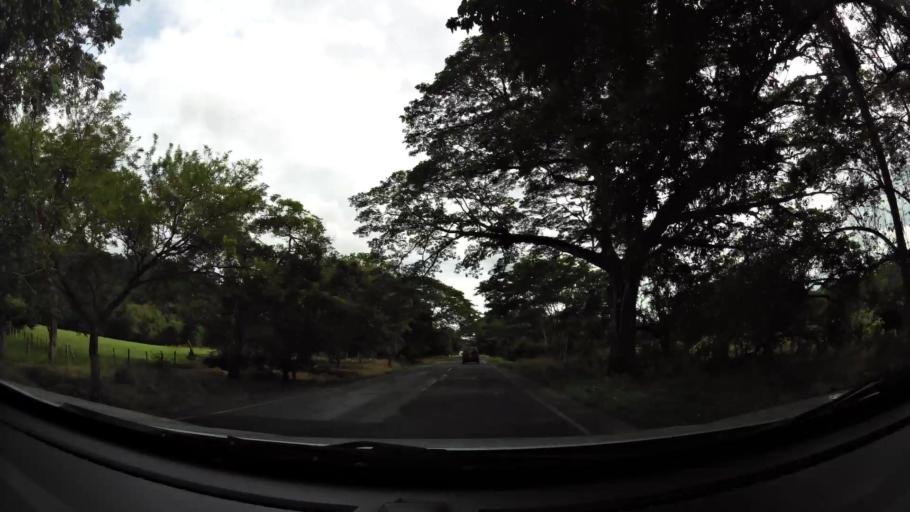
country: CR
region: Guanacaste
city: Juntas
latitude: 10.2283
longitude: -84.9789
